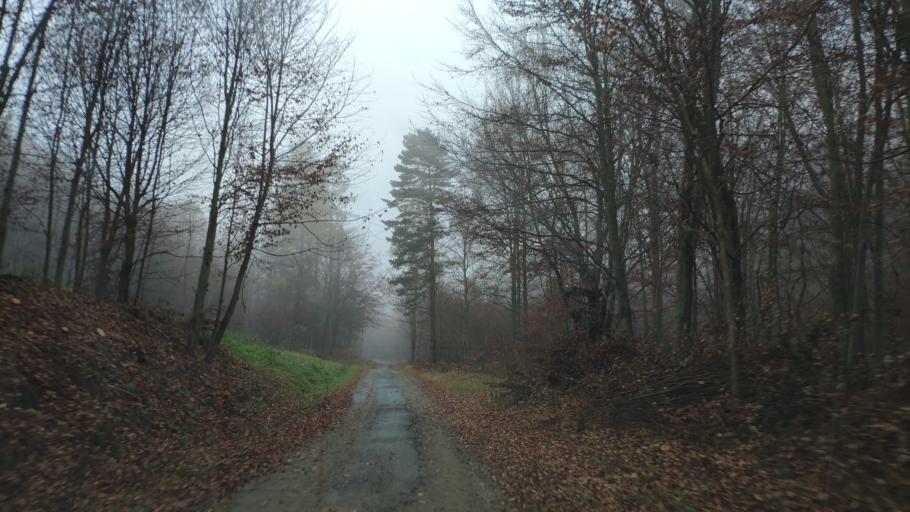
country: SK
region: Presovsky
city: Sabinov
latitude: 49.1541
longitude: 21.2025
